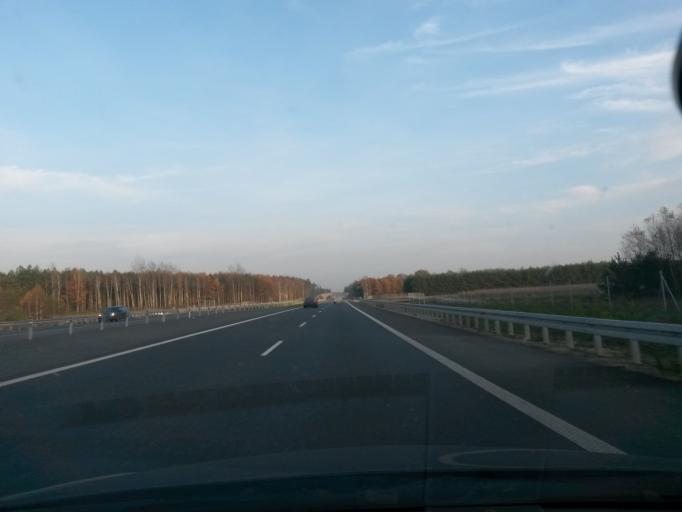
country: PL
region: Lodz Voivodeship
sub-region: Powiat wieruszowski
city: Galewice
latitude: 51.3156
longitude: 18.2644
